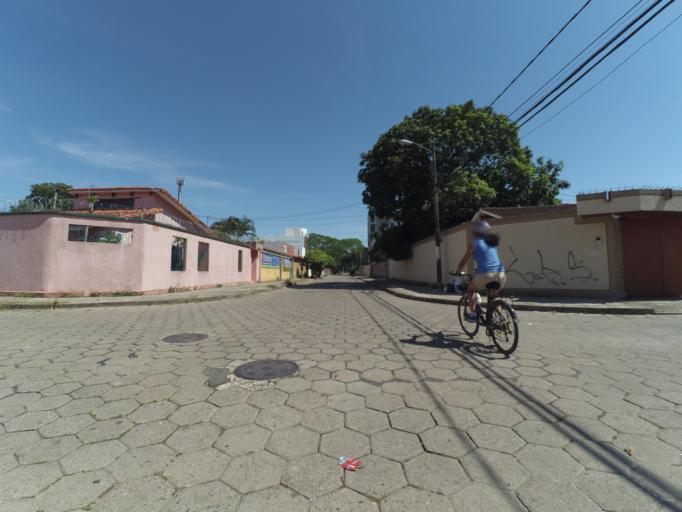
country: BO
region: Santa Cruz
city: Santa Cruz de la Sierra
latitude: -17.7991
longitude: -63.1839
